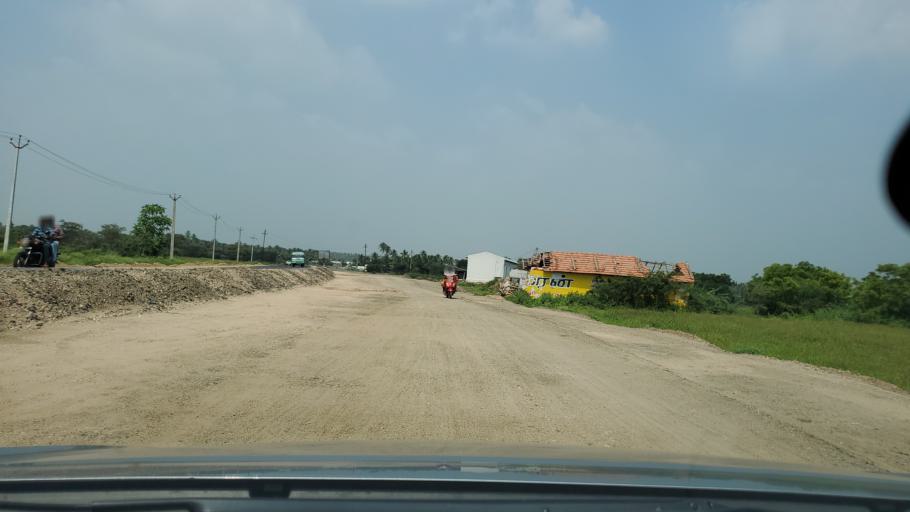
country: IN
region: Tamil Nadu
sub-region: Tiruppur
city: Kangayam
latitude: 10.9200
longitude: 77.4506
